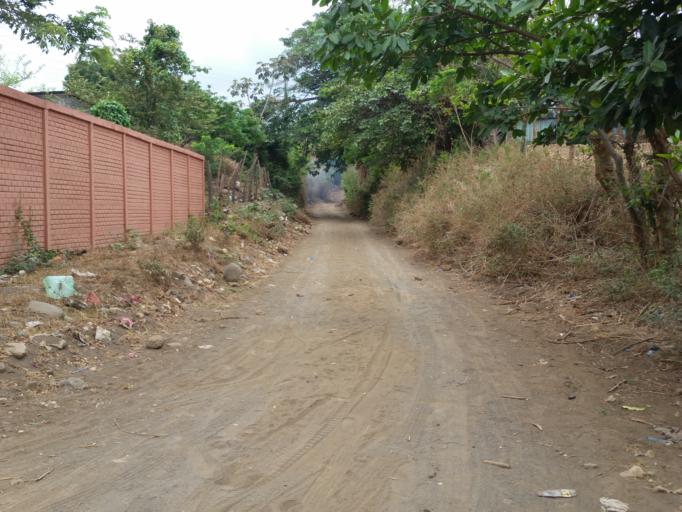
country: NI
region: Managua
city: Managua
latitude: 12.0735
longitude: -86.2541
